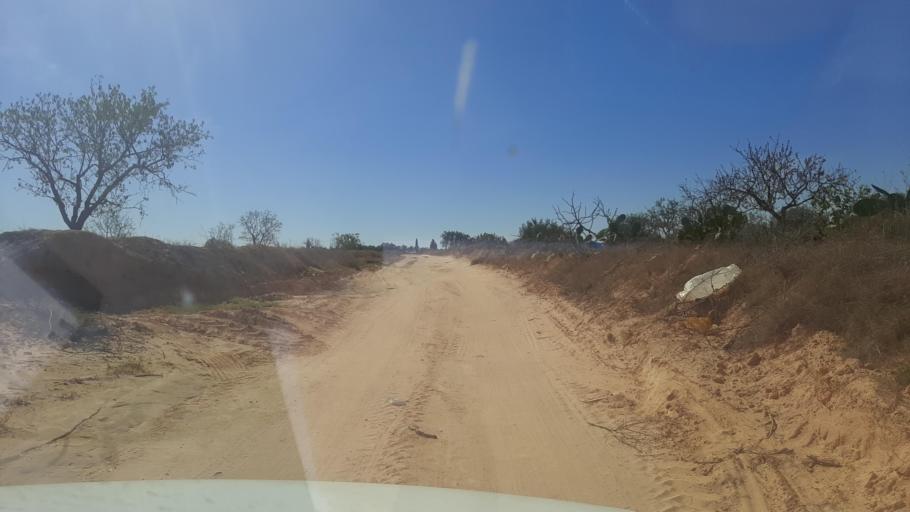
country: TN
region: Safaqis
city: Sfax
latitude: 34.8323
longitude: 10.5568
